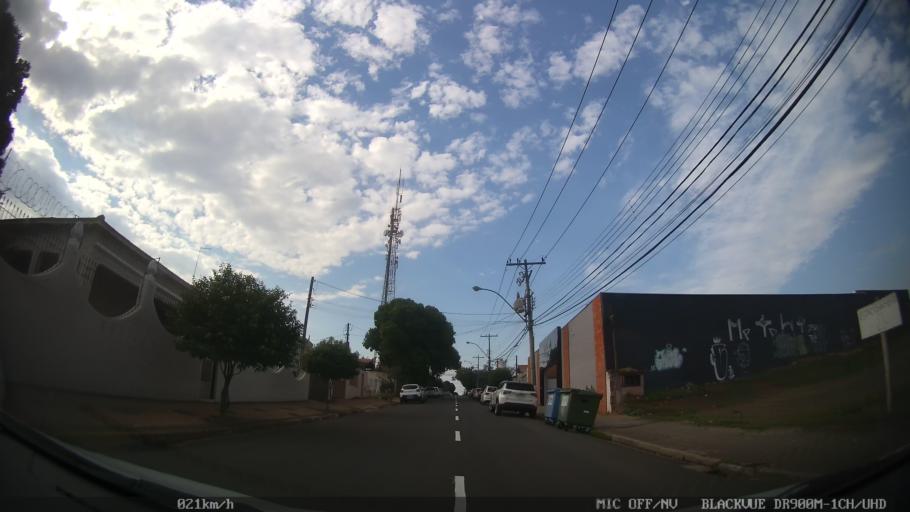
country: BR
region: Sao Paulo
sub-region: Paulinia
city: Paulinia
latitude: -22.7613
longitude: -47.1537
